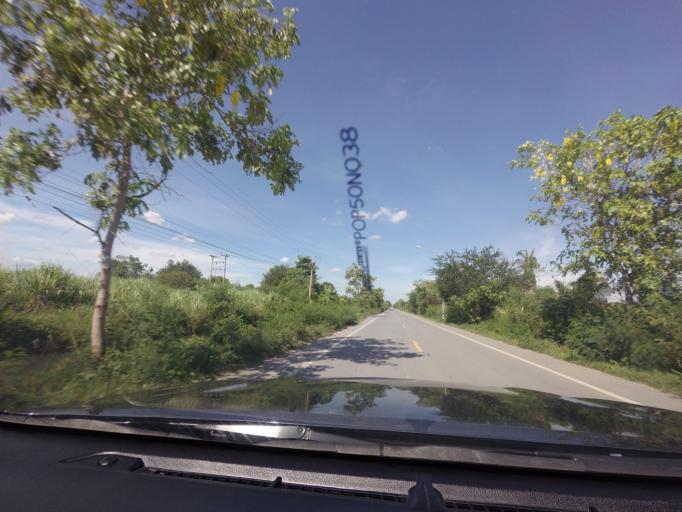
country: TH
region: Suphan Buri
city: Song Phi Nong
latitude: 14.1569
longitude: 99.9910
